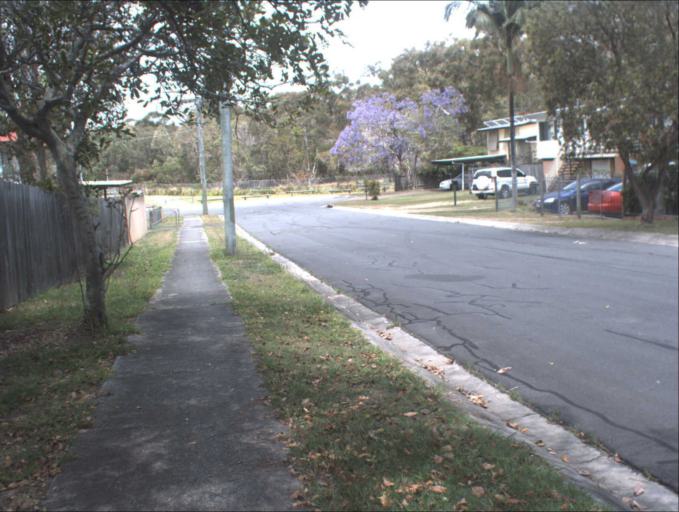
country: AU
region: Queensland
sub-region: Logan
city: Woodridge
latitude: -27.6381
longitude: 153.0953
